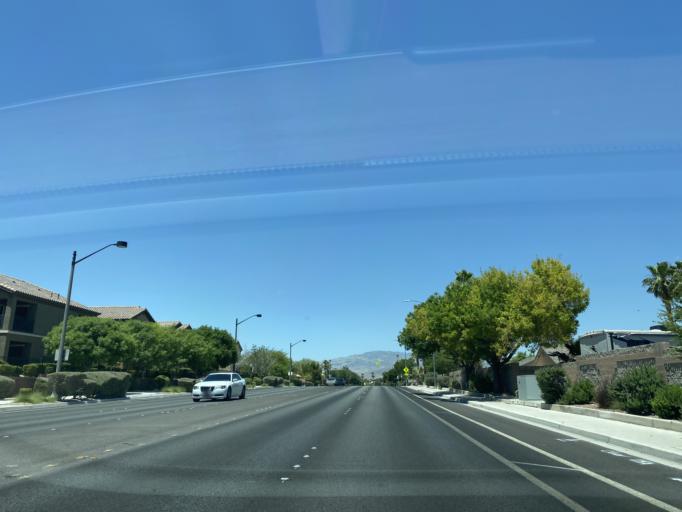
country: US
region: Nevada
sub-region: Clark County
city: Las Vegas
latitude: 36.2863
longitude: -115.2695
